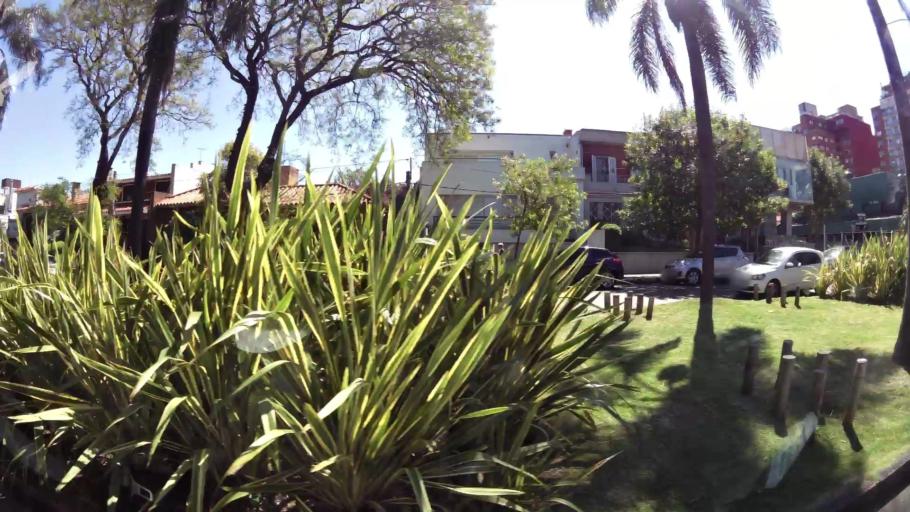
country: UY
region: Montevideo
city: Montevideo
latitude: -34.9069
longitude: -56.1364
